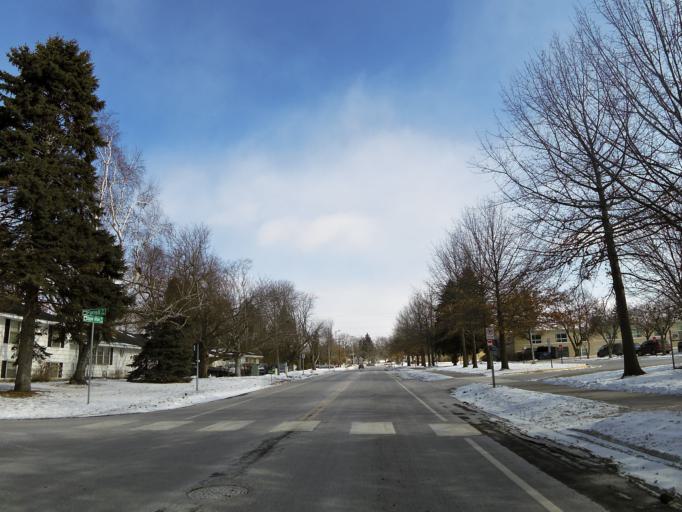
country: US
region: Minnesota
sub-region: Ramsey County
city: Maplewood
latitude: 44.9414
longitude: -92.9879
